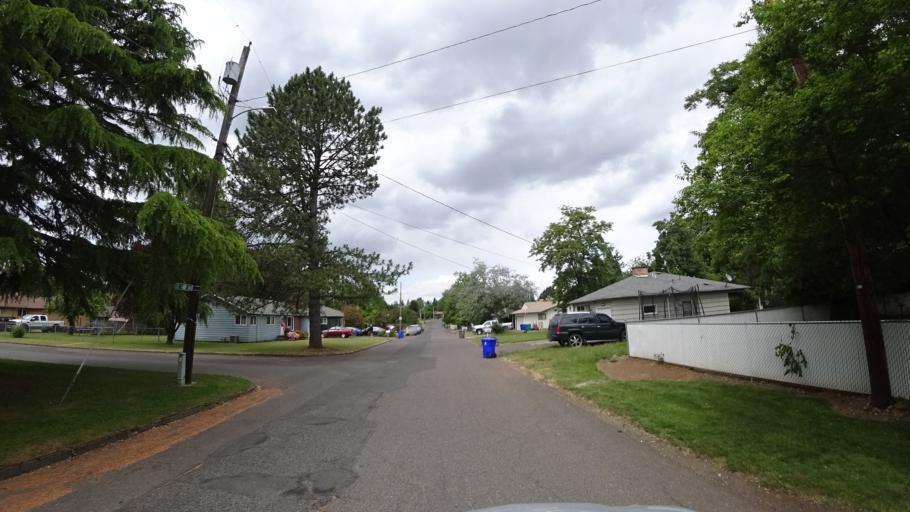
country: US
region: Oregon
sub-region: Clackamas County
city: Happy Valley
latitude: 45.4995
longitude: -122.5164
